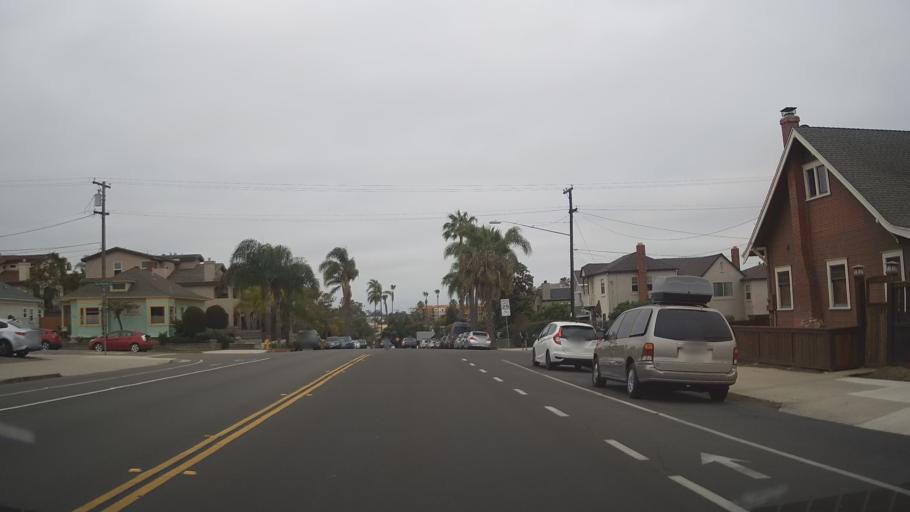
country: US
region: California
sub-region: San Diego County
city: San Diego
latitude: 32.7558
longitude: -117.1500
